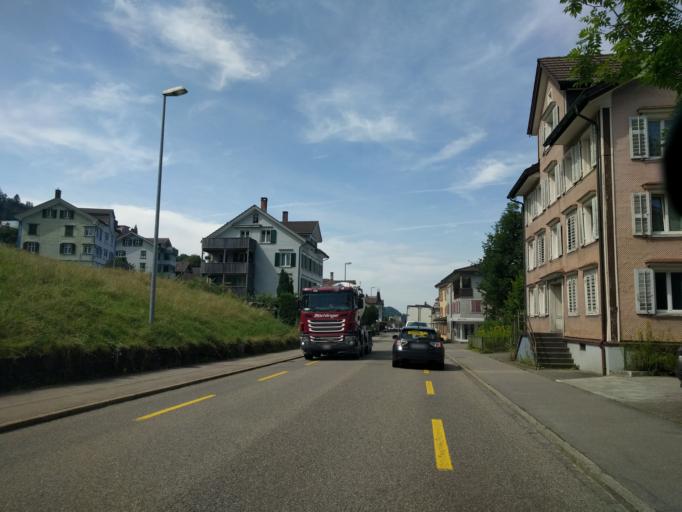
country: CH
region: Saint Gallen
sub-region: Wahlkreis Toggenburg
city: Wattwil
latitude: 47.2969
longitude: 9.0863
